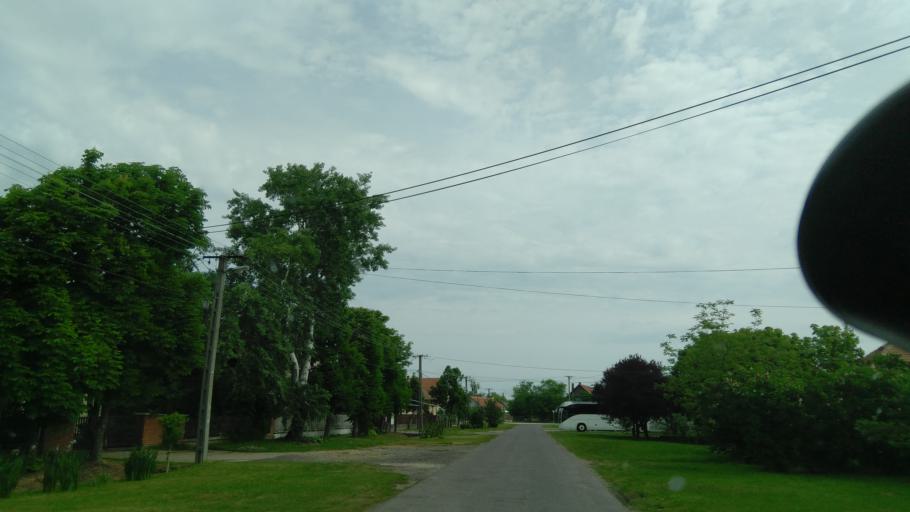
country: HU
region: Bekes
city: Szeghalom
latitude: 47.0225
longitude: 21.1690
